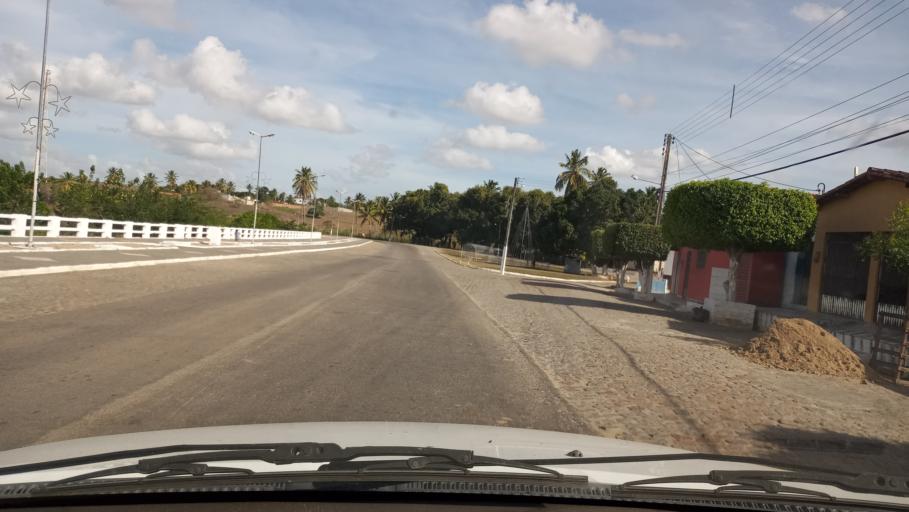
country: BR
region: Rio Grande do Norte
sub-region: Goianinha
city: Goianinha
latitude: -6.3315
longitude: -35.3064
